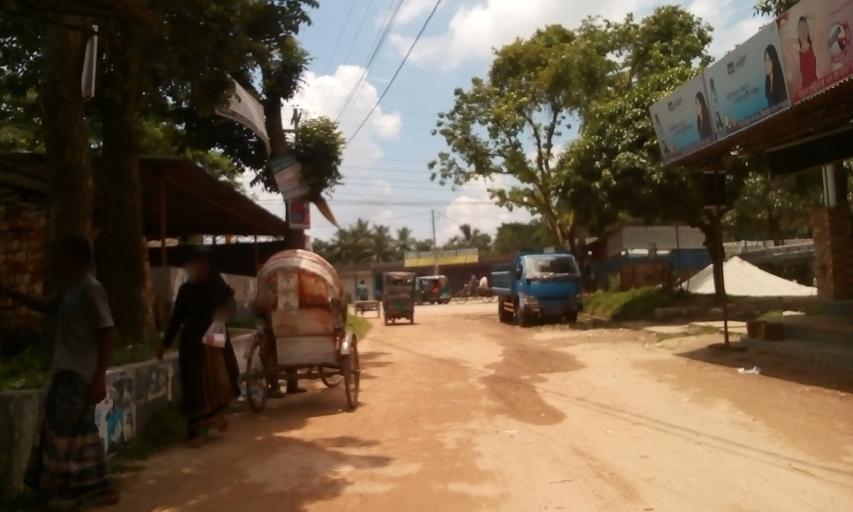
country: IN
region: West Bengal
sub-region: Dakshin Dinajpur
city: Balurghat
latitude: 25.3854
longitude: 88.9884
